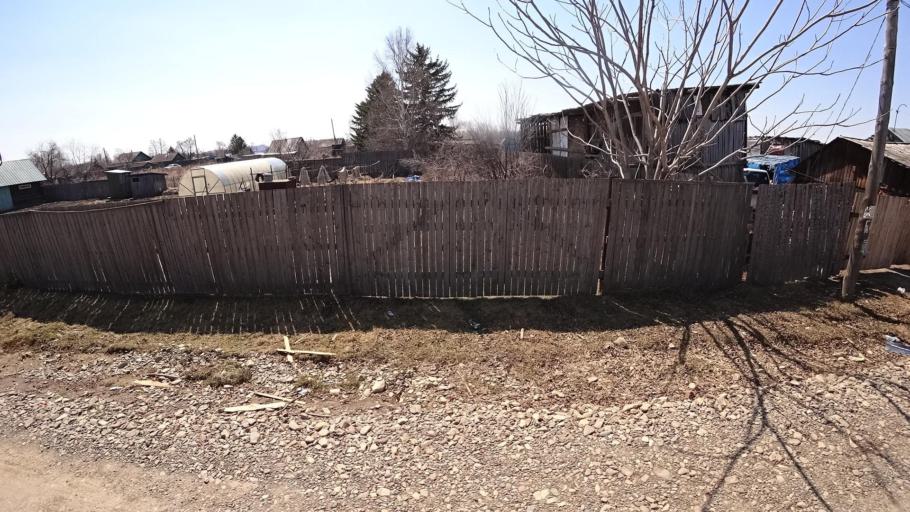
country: RU
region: Khabarovsk Krai
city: Khurba
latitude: 50.4123
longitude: 136.8664
